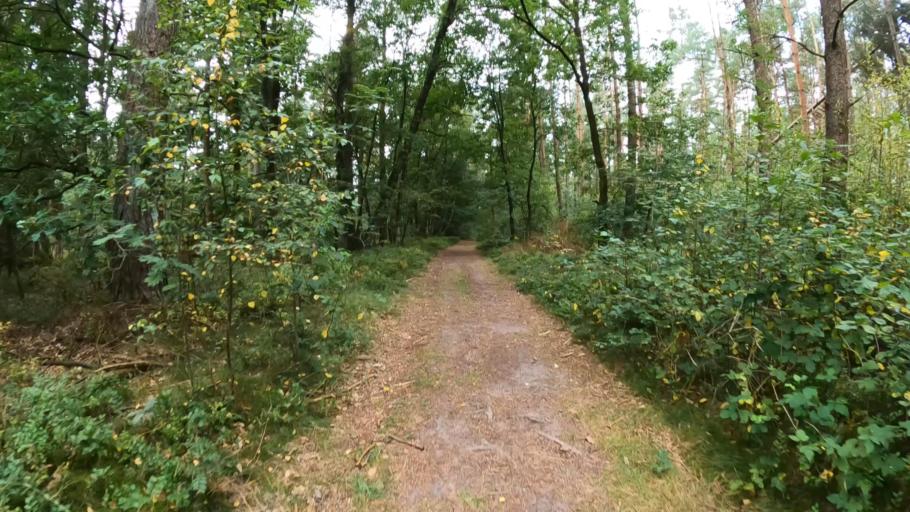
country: DE
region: Lower Saxony
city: Neu Wulmstorf
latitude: 53.4303
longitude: 9.8318
